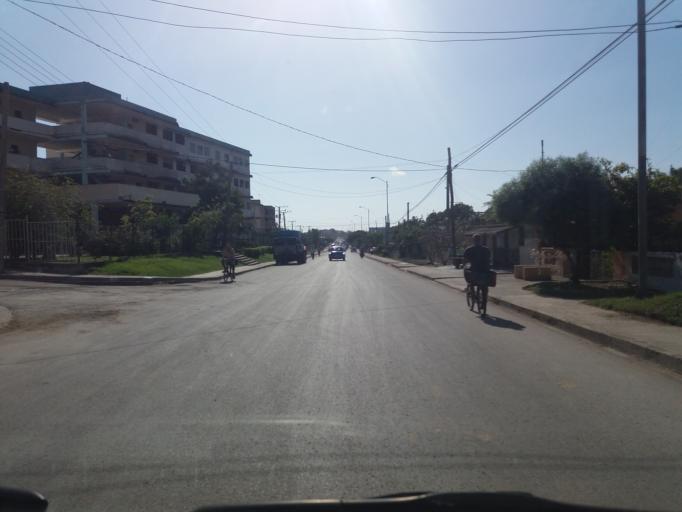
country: CU
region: Cienfuegos
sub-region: Municipio de Cienfuegos
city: Cienfuegos
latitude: 22.1552
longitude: -80.4334
